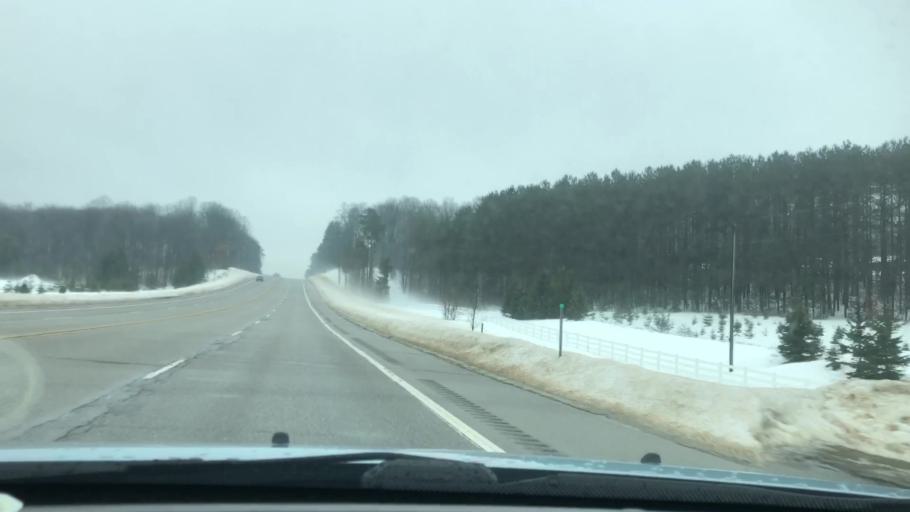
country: US
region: Michigan
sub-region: Otsego County
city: Gaylord
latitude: 45.0521
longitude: -84.7759
